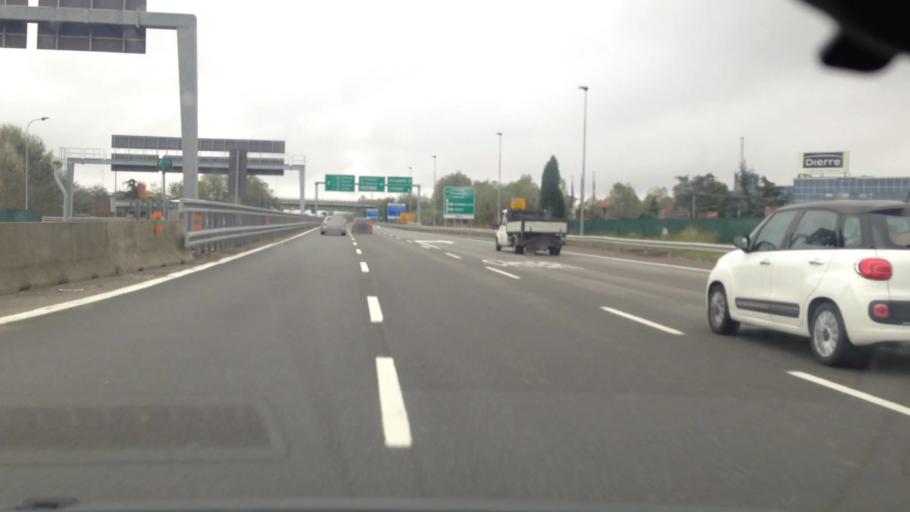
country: IT
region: Piedmont
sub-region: Provincia di Asti
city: Villanova d'Asti
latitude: 44.9534
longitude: 7.9211
